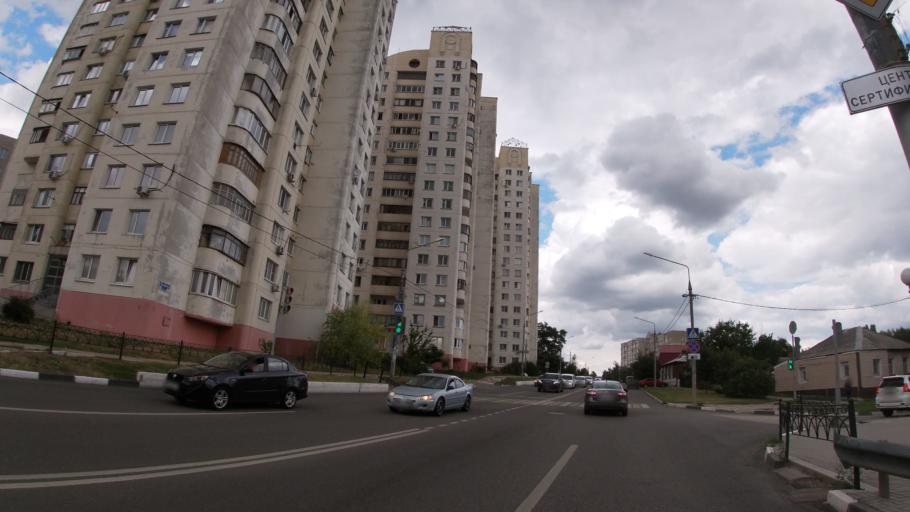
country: RU
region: Belgorod
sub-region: Belgorodskiy Rayon
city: Belgorod
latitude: 50.6003
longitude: 36.6079
